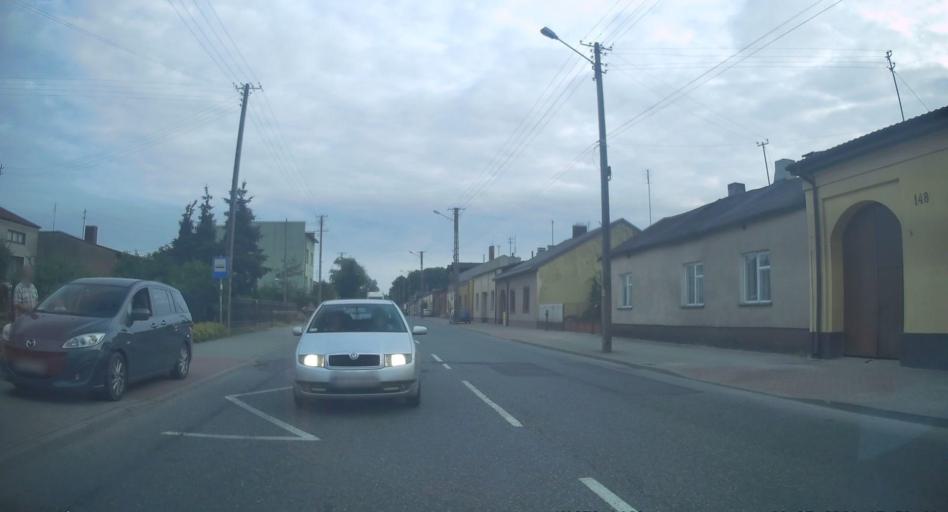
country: PL
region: Lodz Voivodeship
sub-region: Powiat radomszczanski
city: Kamiensk
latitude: 51.1928
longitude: 19.4983
